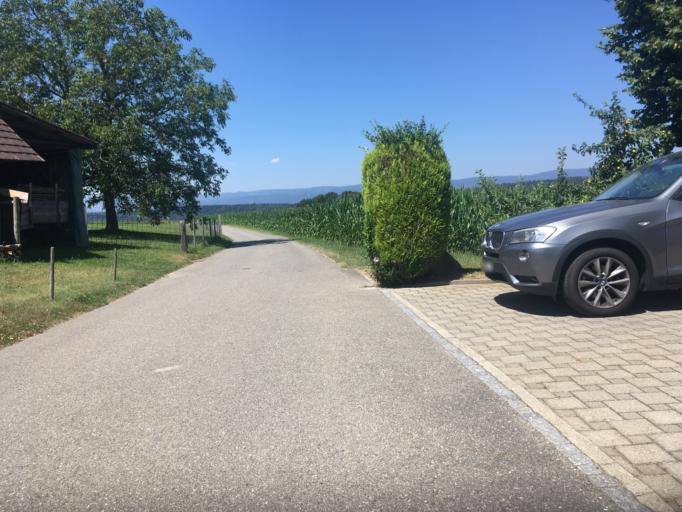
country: CH
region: Solothurn
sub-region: Bezirk Bucheggberg
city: Messen
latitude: 47.0767
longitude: 7.4166
